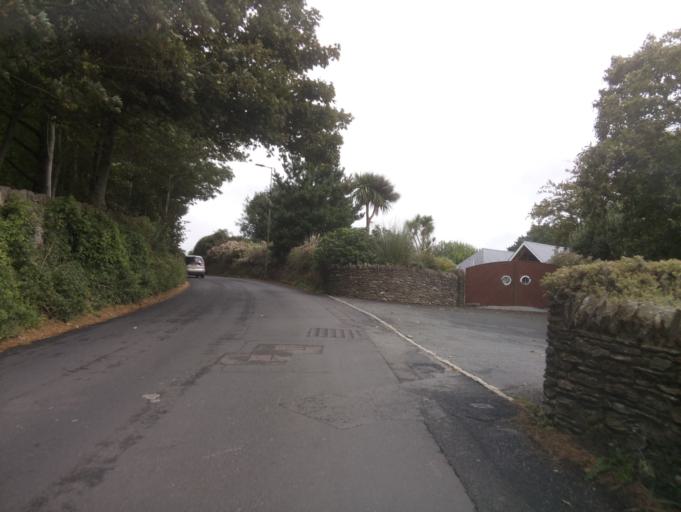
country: GB
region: England
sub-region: Devon
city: Dartmouth
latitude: 50.3219
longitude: -3.5981
